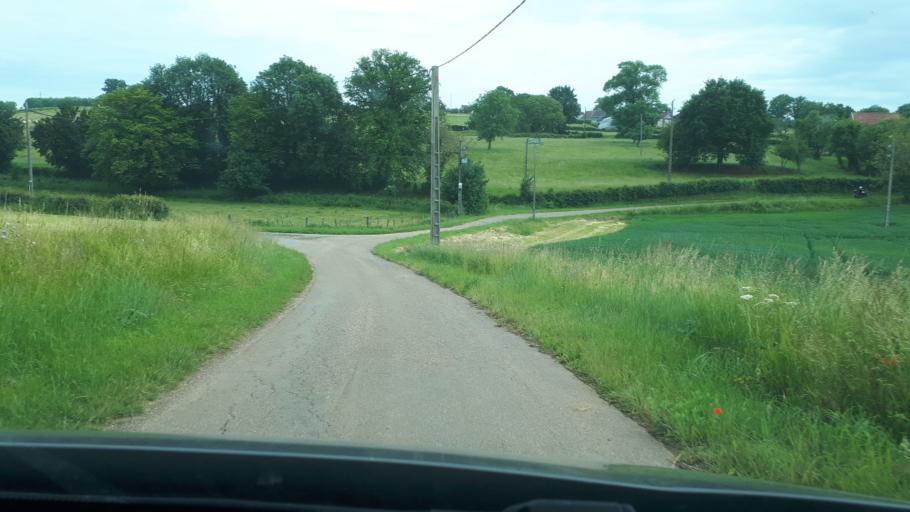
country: FR
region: Centre
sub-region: Departement du Cher
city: Sancerre
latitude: 47.3187
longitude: 2.7293
